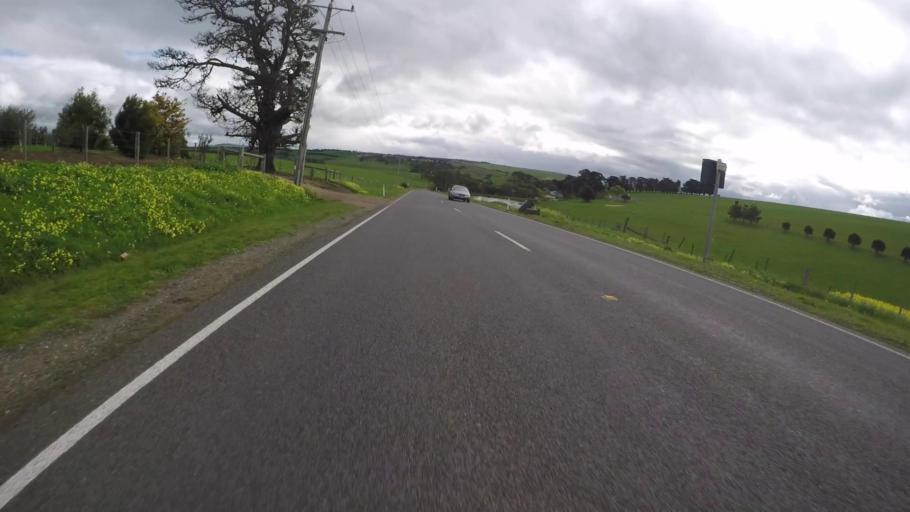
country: AU
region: Victoria
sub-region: Greater Geelong
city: Wandana Heights
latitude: -38.1732
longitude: 144.2643
